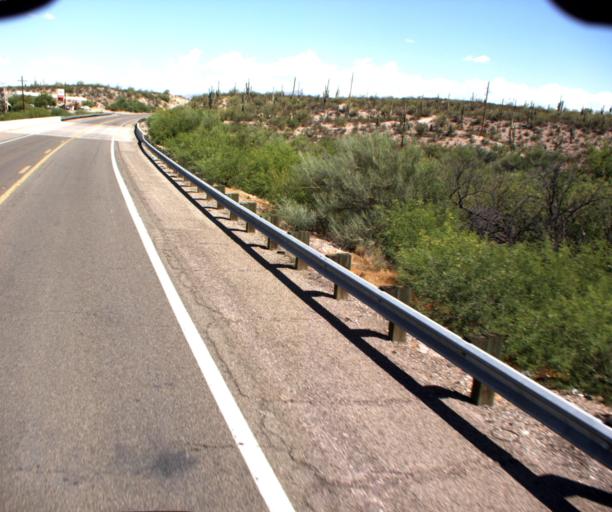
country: US
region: Arizona
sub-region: Pinal County
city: Kearny
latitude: 32.9310
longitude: -110.7336
